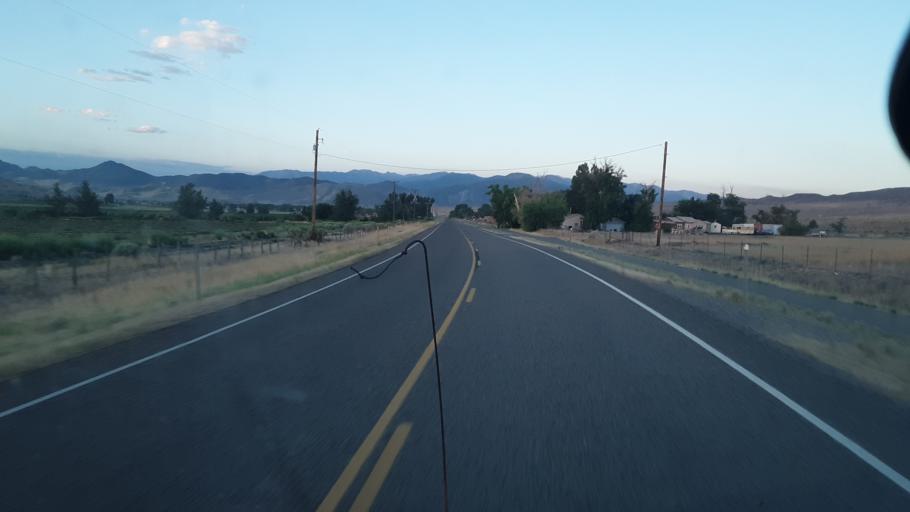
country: US
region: Utah
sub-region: Sevier County
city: Monroe
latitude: 38.6499
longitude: -112.2095
